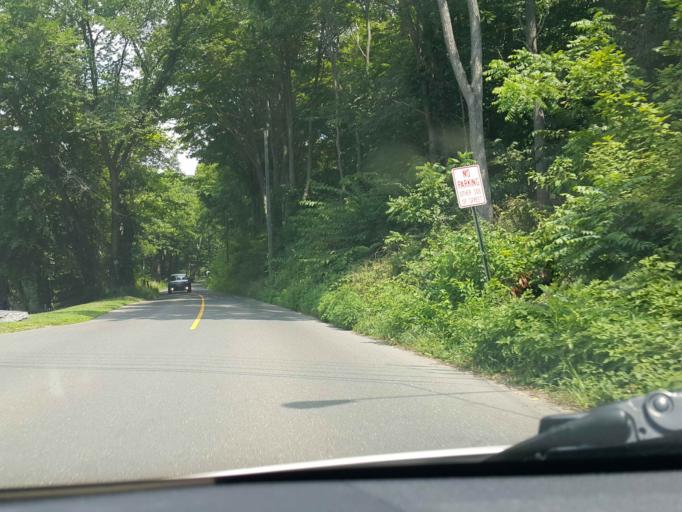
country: US
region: Connecticut
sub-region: New Haven County
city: Guilford
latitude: 41.2897
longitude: -72.6886
